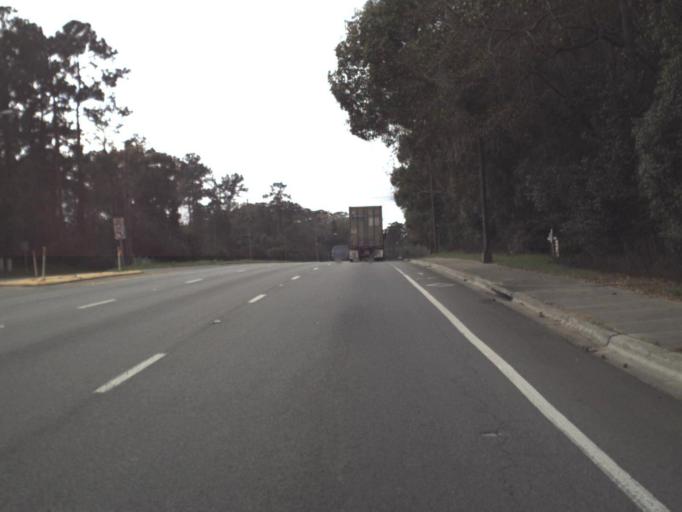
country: US
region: Florida
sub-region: Leon County
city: Tallahassee
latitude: 30.5176
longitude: -84.2408
